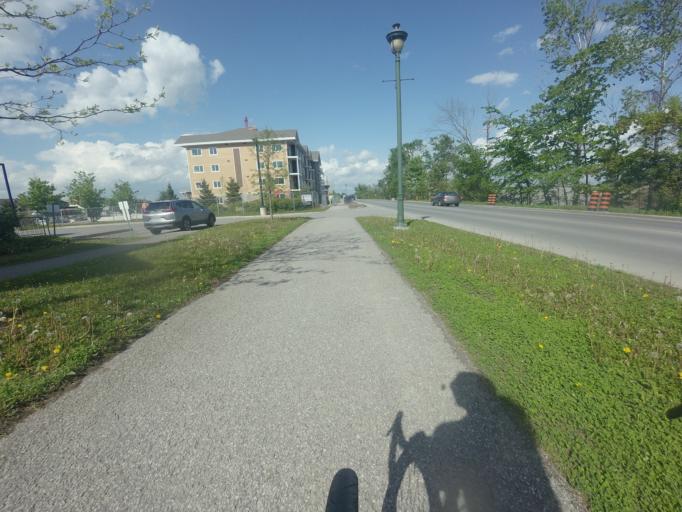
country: CA
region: Ontario
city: Carleton Place
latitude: 45.1377
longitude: -76.1309
